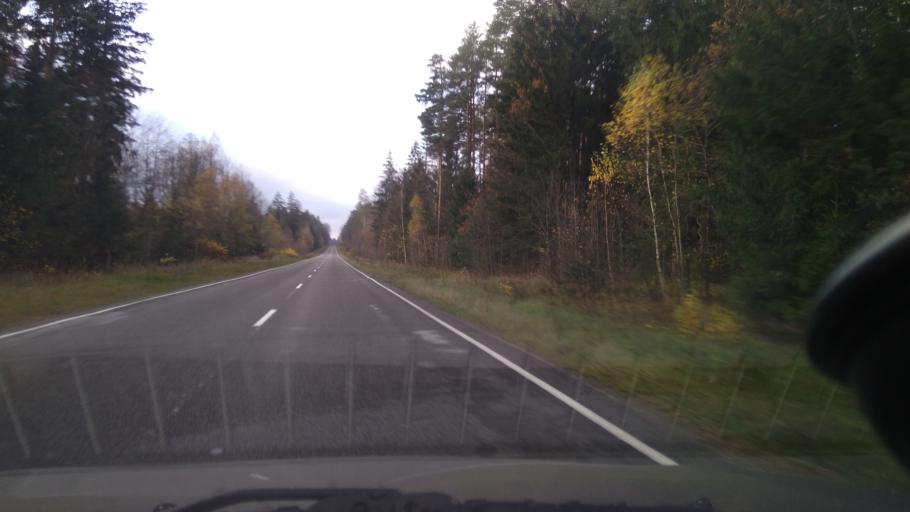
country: BY
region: Minsk
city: Urechcha
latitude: 53.2086
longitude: 27.9486
